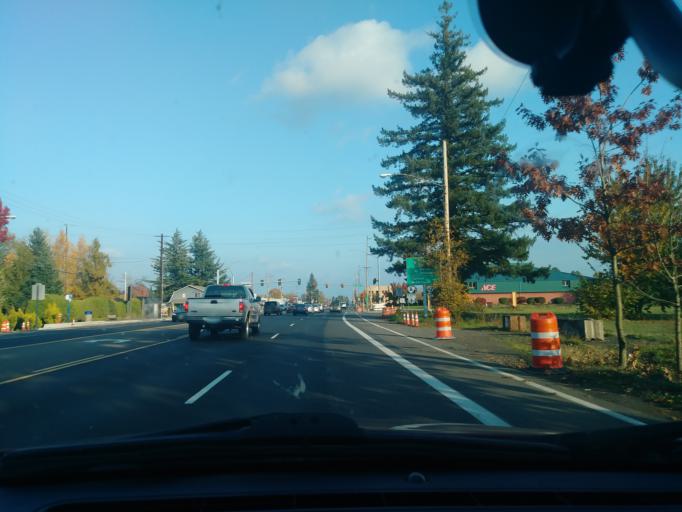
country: US
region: Oregon
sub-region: Washington County
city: Forest Grove
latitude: 45.5201
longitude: -123.0858
